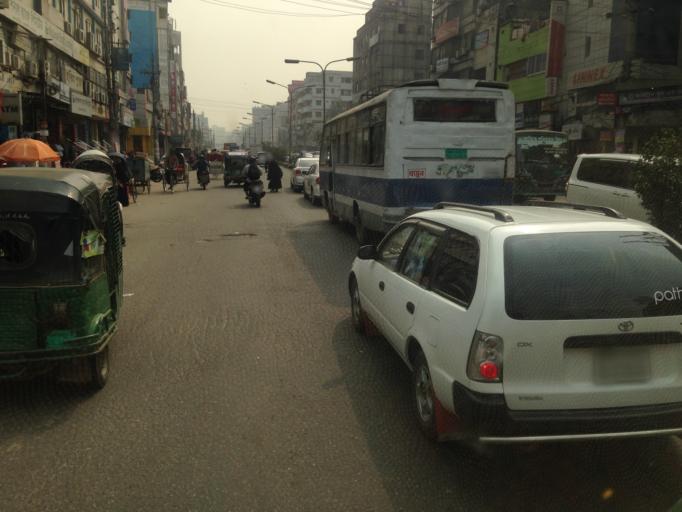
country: BD
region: Dhaka
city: Tungi
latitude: 23.8165
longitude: 90.4211
